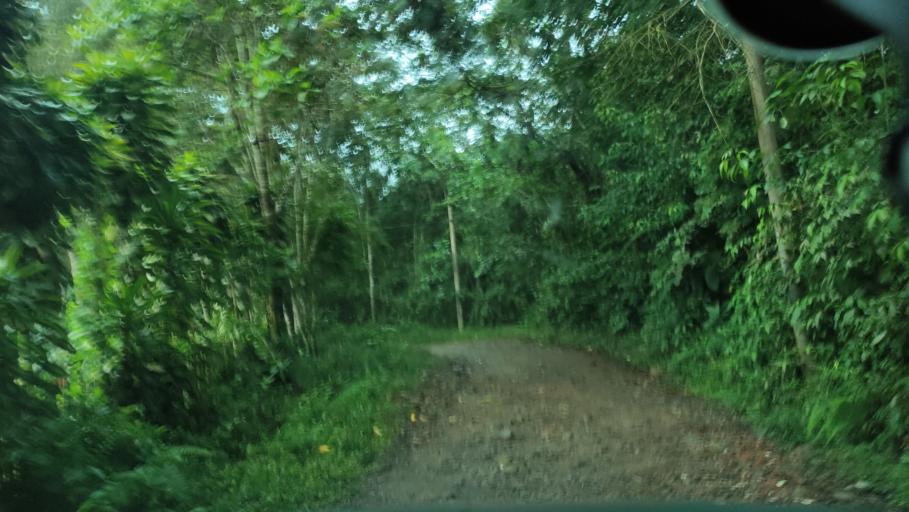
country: CO
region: Valle del Cauca
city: Jamundi
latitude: 3.3226
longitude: -76.6333
